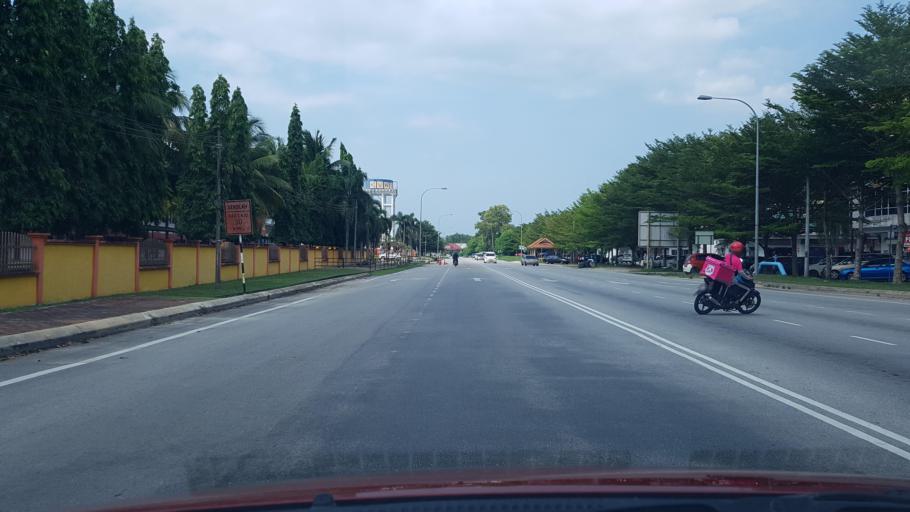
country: MY
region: Terengganu
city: Kuala Terengganu
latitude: 5.3577
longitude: 103.0944
